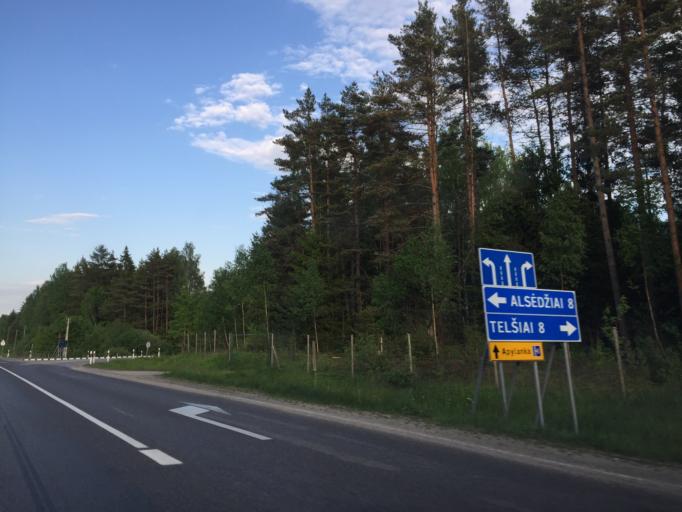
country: LT
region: Telsiu apskritis
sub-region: Telsiai
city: Telsiai
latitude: 56.0014
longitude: 22.1461
